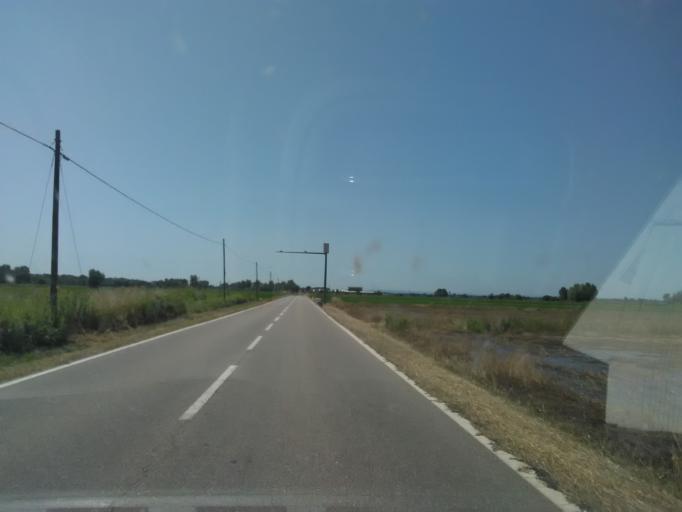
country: IT
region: Piedmont
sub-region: Provincia di Vercelli
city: Greggio
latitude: 45.4445
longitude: 8.3839
